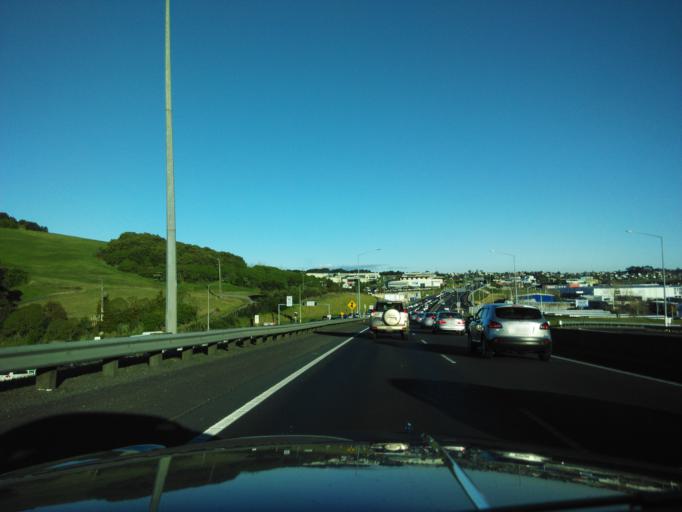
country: NZ
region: Auckland
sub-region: Auckland
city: Rothesay Bay
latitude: -36.7349
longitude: 174.7176
